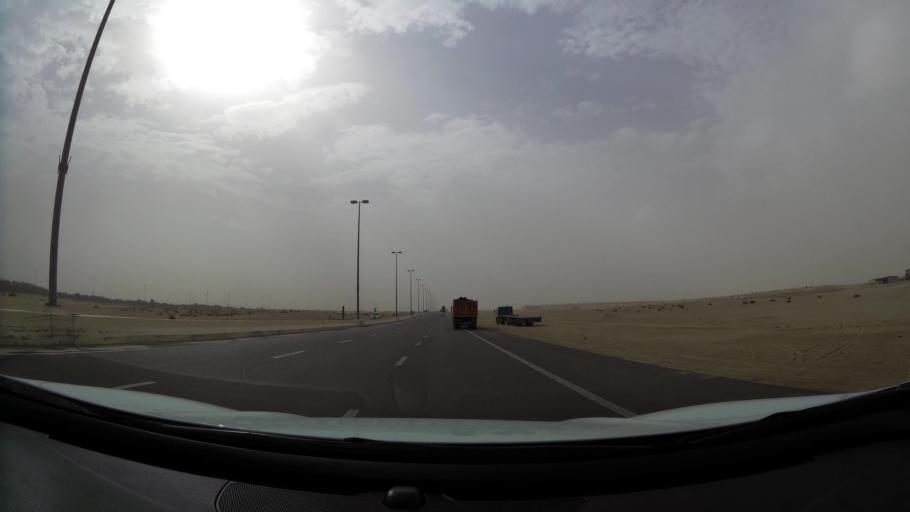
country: AE
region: Abu Dhabi
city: Abu Dhabi
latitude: 24.4714
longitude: 54.6710
